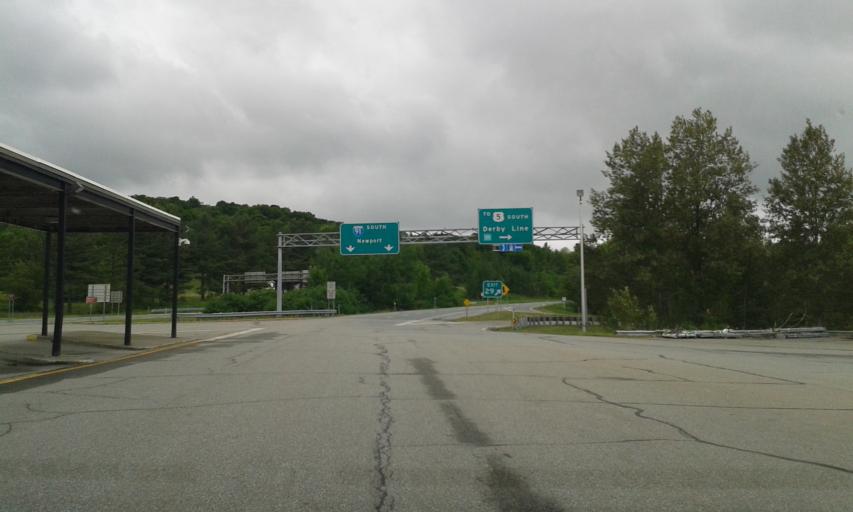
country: US
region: Vermont
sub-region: Orleans County
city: Newport
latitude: 45.0044
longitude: -72.0896
